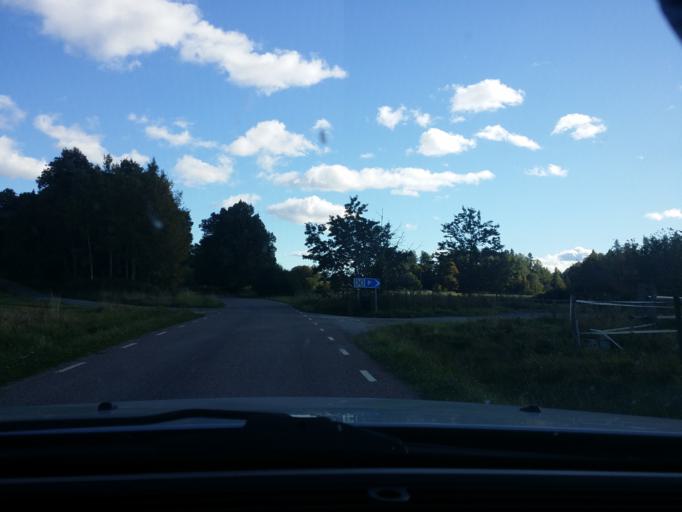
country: SE
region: Vaestmanland
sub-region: Vasteras
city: Vasteras
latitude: 59.5371
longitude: 16.4751
